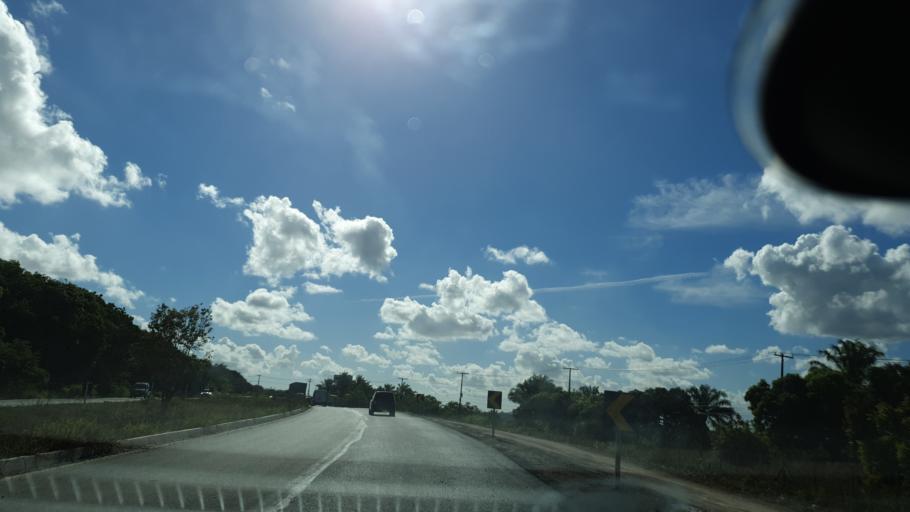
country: BR
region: Bahia
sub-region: Camacari
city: Camacari
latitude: -12.6804
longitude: -38.2853
